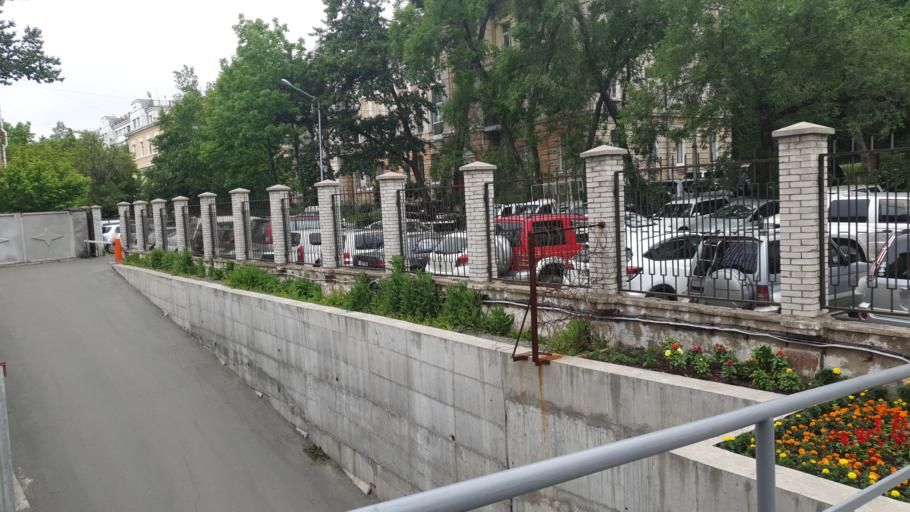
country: RU
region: Primorskiy
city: Vladivostok
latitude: 43.1118
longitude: 131.9142
